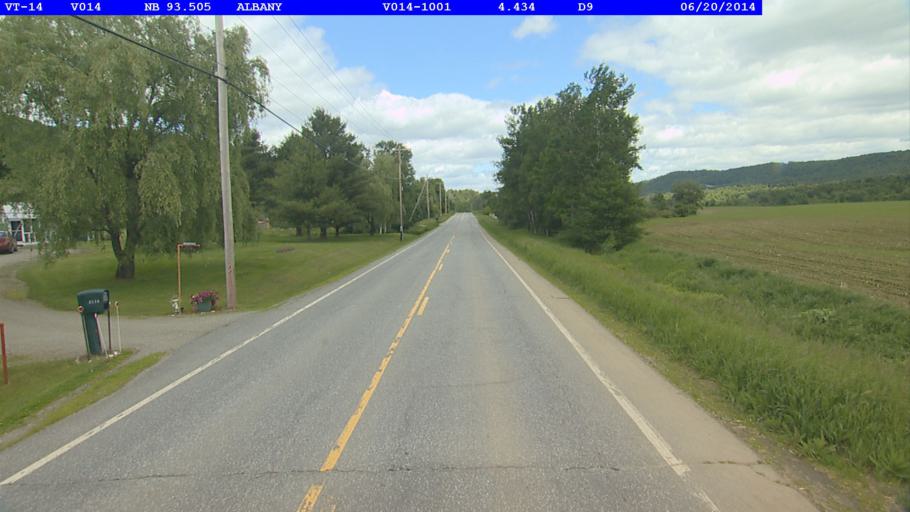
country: US
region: Vermont
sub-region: Orleans County
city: Newport
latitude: 44.7593
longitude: -72.3561
